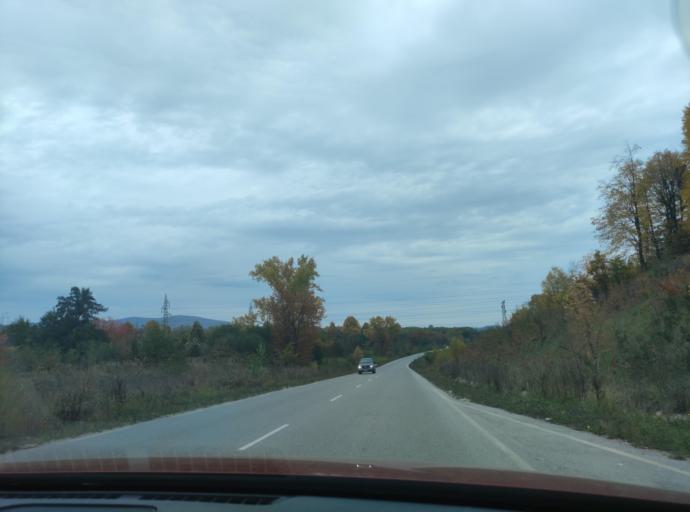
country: BG
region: Montana
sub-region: Obshtina Berkovitsa
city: Berkovitsa
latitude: 43.2326
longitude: 23.1587
